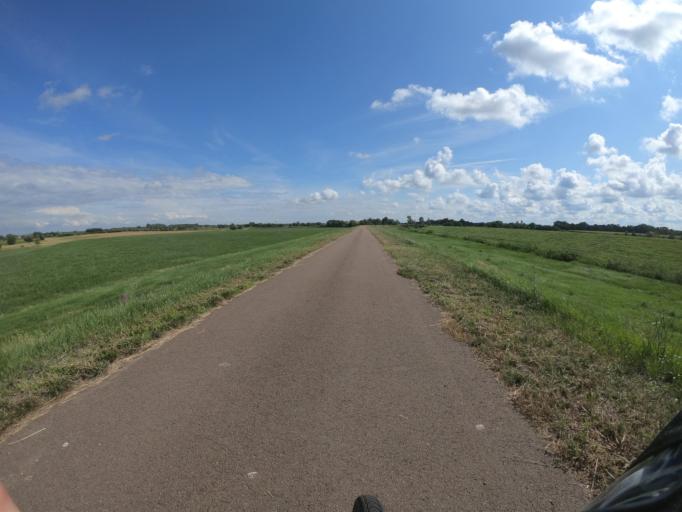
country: HU
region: Heves
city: Poroszlo
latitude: 47.7007
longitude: 20.6865
